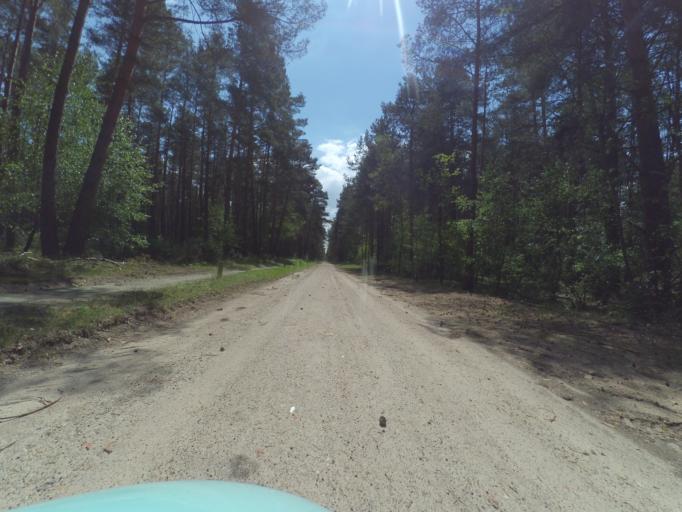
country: DE
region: Lower Saxony
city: Ummern
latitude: 52.6237
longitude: 10.4468
